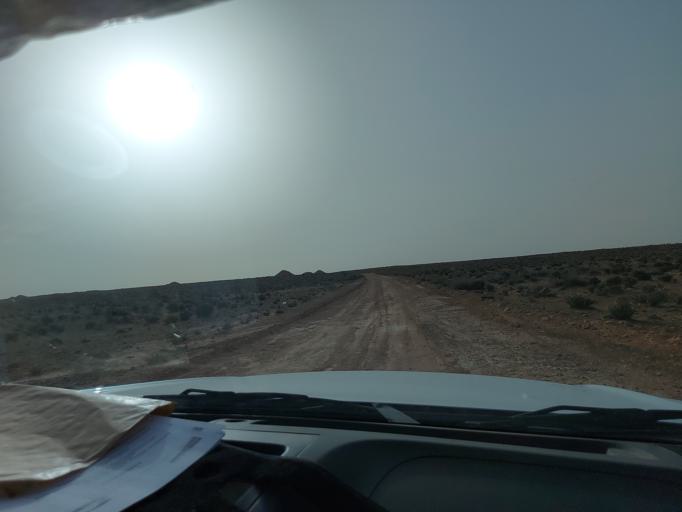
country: TN
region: Madanin
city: Medenine
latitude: 33.2862
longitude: 10.5962
